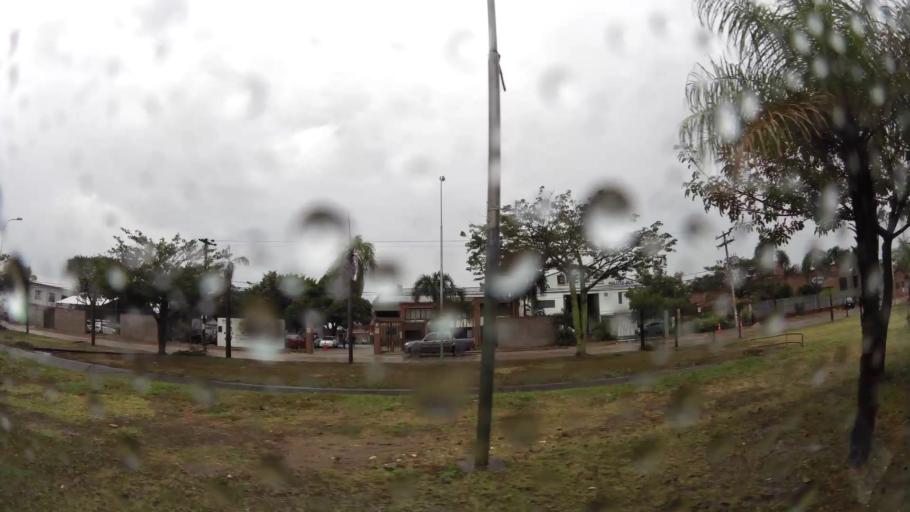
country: BO
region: Santa Cruz
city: Santa Cruz de la Sierra
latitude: -17.8159
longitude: -63.2242
